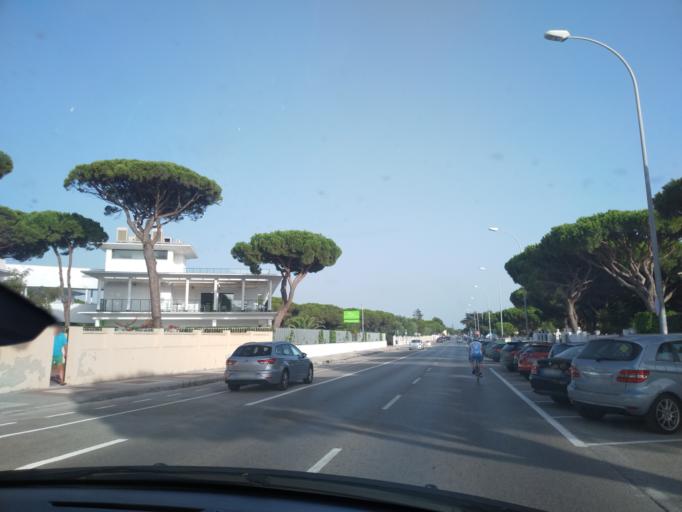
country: ES
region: Andalusia
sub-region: Provincia de Cadiz
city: Chiclana de la Frontera
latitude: 36.3747
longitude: -6.1848
